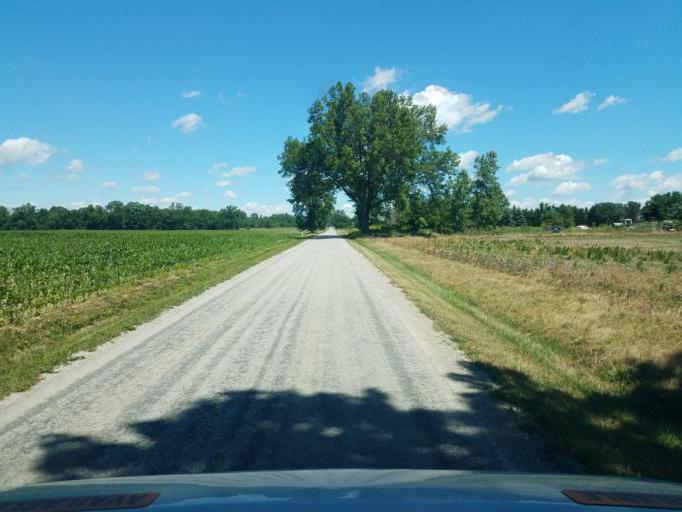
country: US
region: Ohio
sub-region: Crawford County
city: Bucyrus
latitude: 40.6686
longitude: -82.9388
